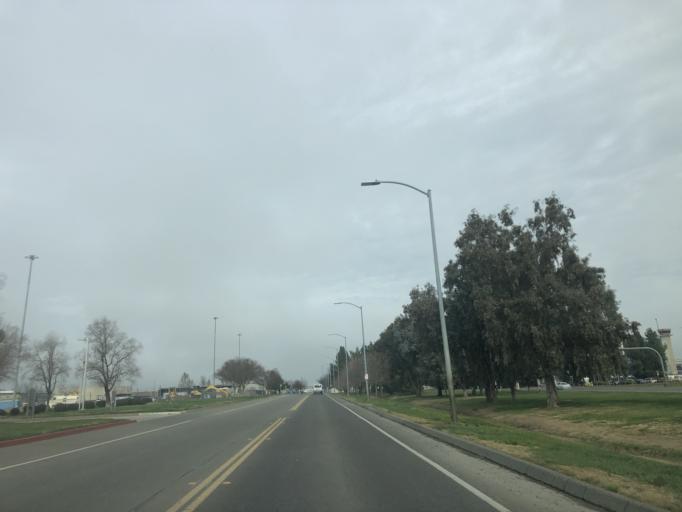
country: US
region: California
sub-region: Yolo County
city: West Sacramento
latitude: 38.6860
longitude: -121.5947
